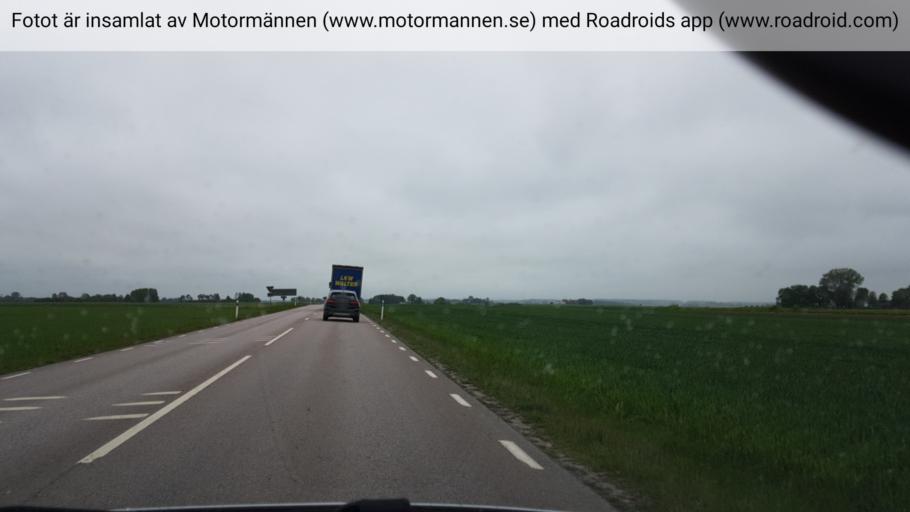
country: SE
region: Vaestra Goetaland
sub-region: Lidkopings Kommun
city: Lidkoping
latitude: 58.4813
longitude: 13.1053
